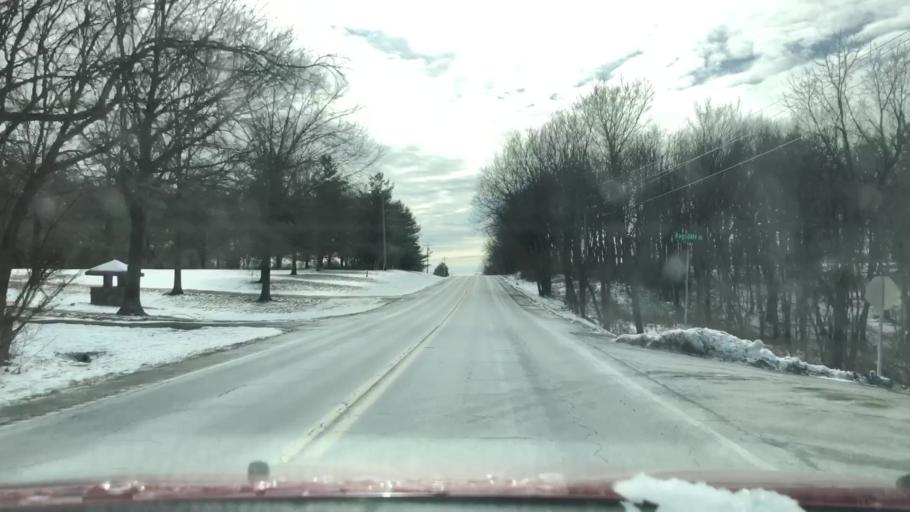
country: US
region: Missouri
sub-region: Jackson County
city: Lone Jack
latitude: 38.8853
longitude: -94.1347
